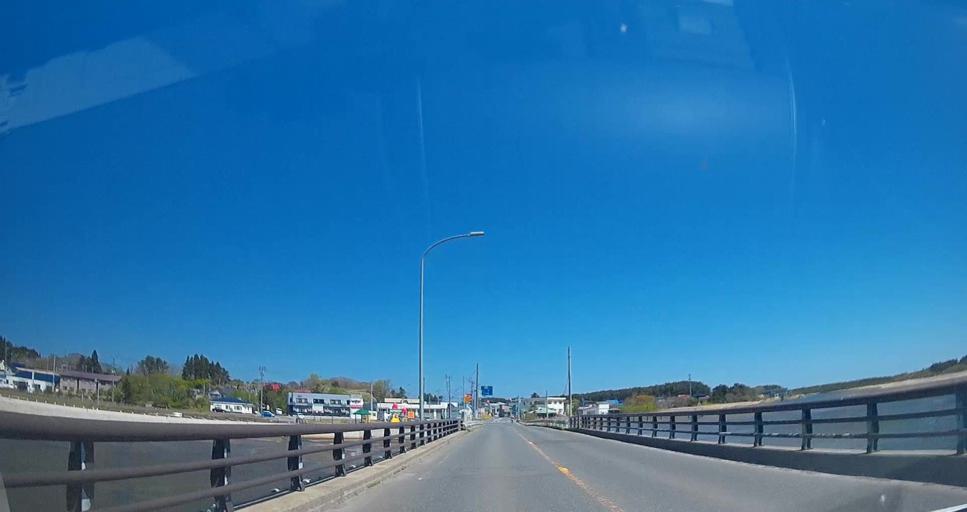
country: JP
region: Aomori
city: Misawa
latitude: 40.9587
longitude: 141.3718
